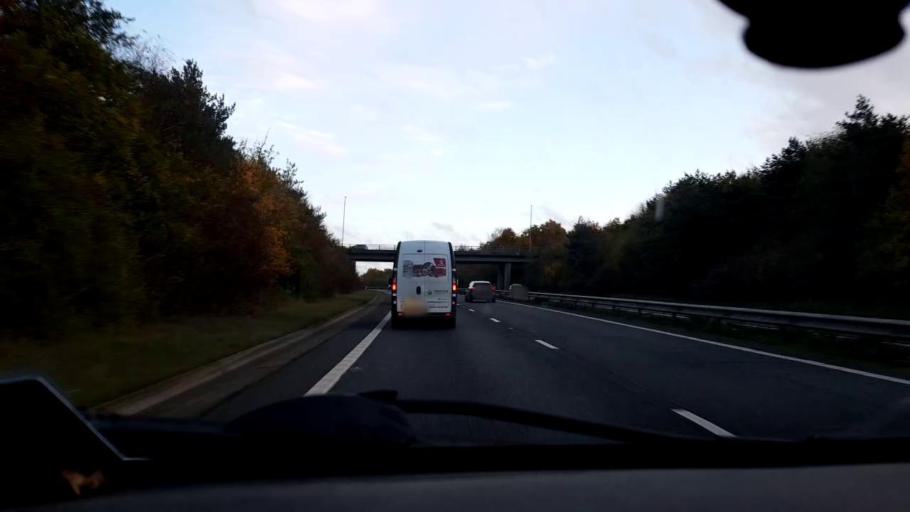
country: GB
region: England
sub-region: Norfolk
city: Bowthorpe
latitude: 52.6265
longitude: 1.1963
